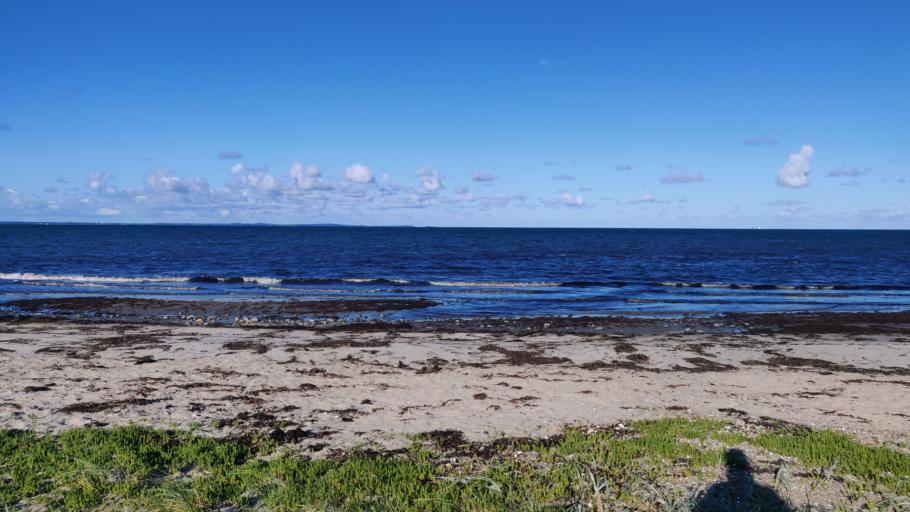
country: SE
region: Skane
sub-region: Hoganas Kommun
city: Hoganas
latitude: 56.1644
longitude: 12.5636
